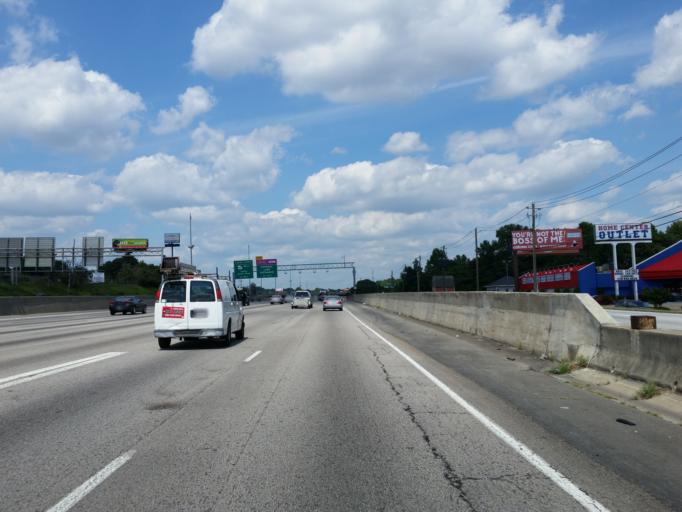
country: US
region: Georgia
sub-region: DeKalb County
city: Doraville
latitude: 33.8981
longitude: -84.2486
